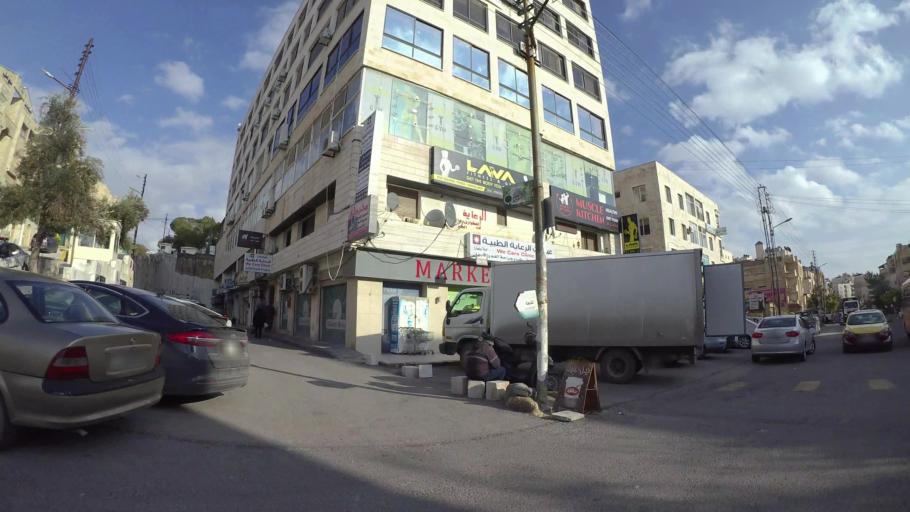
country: JO
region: Amman
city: Al Jubayhah
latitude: 31.9823
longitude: 35.8756
